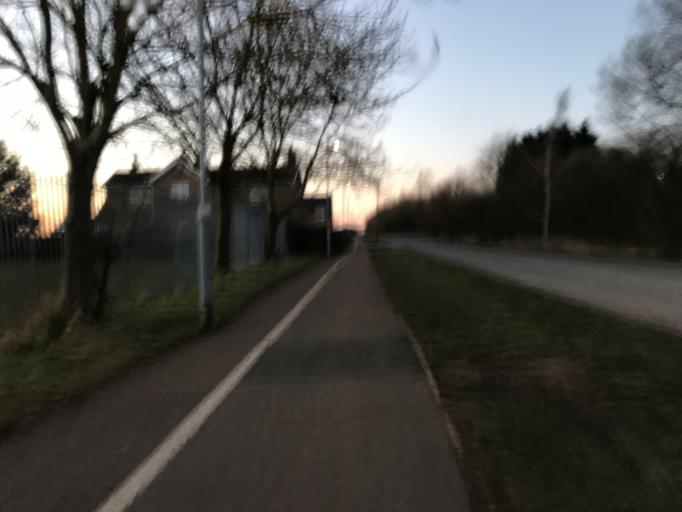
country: GB
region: England
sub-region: North East Lincolnshire
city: Waltham
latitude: 53.5241
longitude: -0.0777
